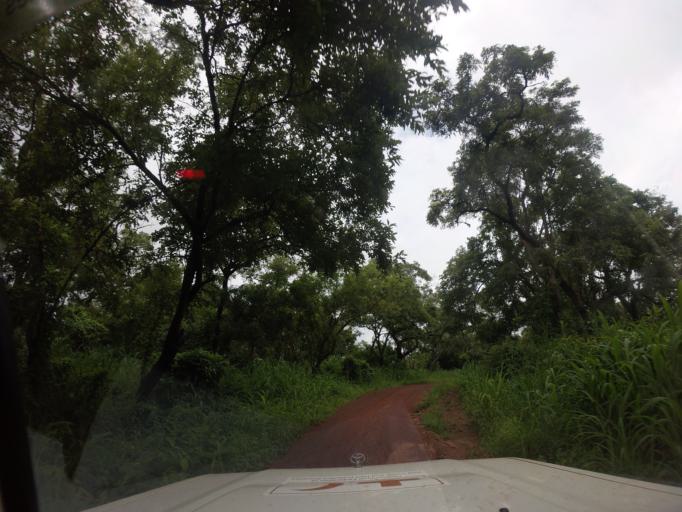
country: SL
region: Northern Province
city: Kamakwie
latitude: 9.6836
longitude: -12.2427
